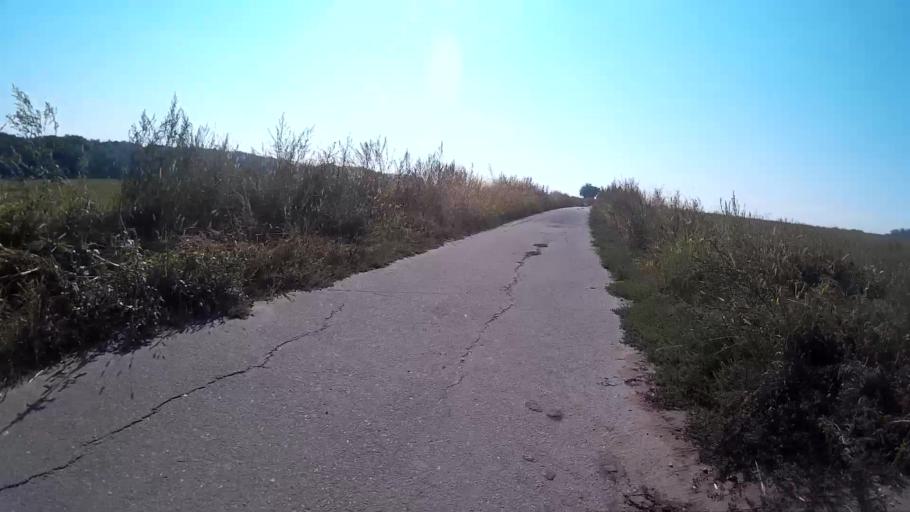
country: CZ
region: South Moravian
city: Novosedly
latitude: 48.8608
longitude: 16.5342
